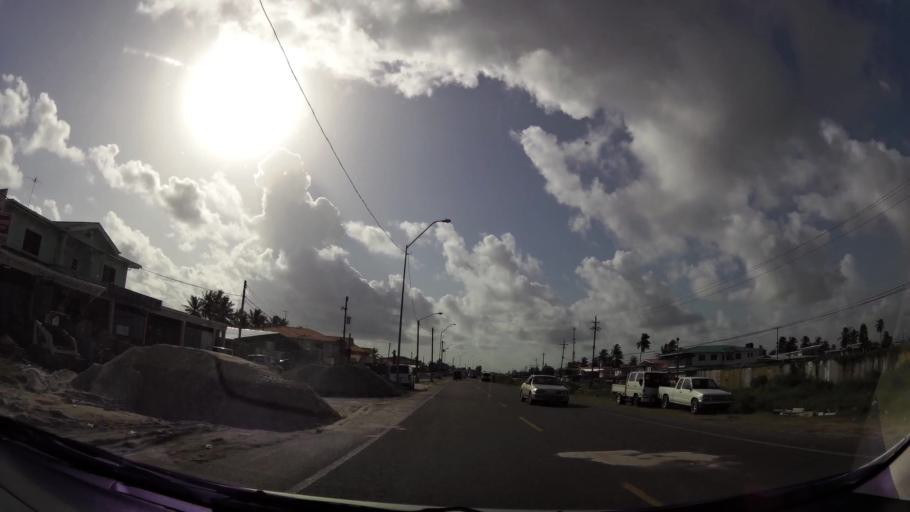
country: GY
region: Demerara-Mahaica
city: Georgetown
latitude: 6.8118
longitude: -58.0626
